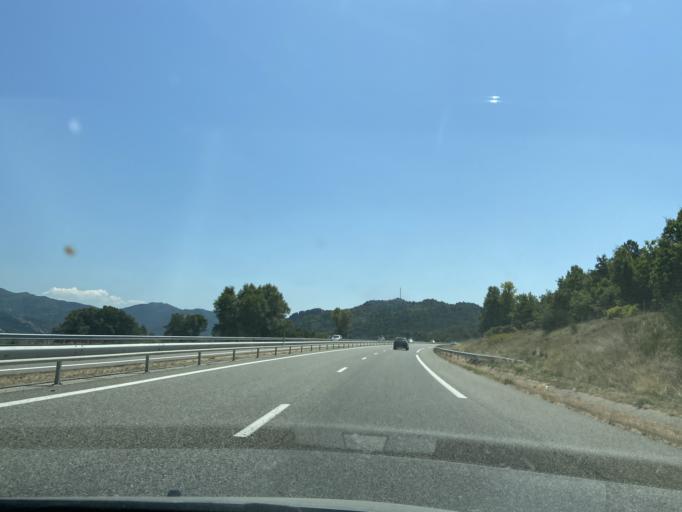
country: FR
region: Provence-Alpes-Cote d'Azur
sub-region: Departement des Alpes-de-Haute-Provence
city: Volonne
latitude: 44.1050
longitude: 5.9937
